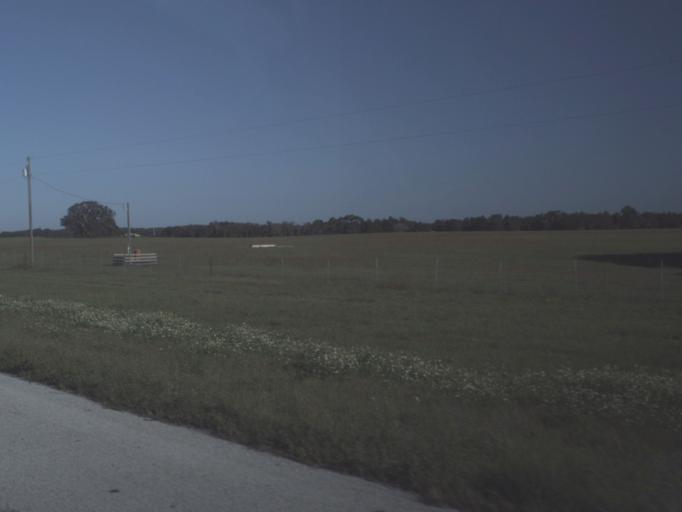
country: US
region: Florida
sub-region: Sumter County
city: Wildwood
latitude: 28.7847
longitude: -81.9774
